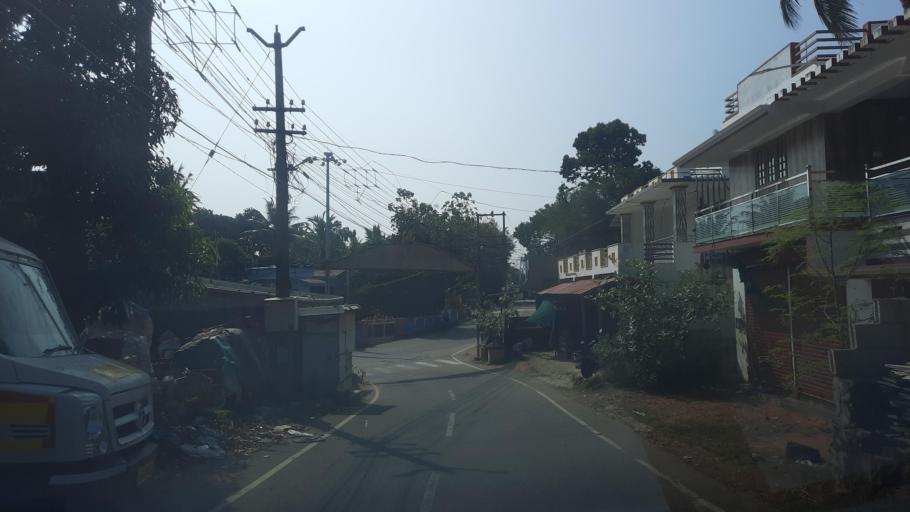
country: IN
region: Kerala
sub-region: Thiruvananthapuram
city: Nedumangad
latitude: 8.5793
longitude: 76.9266
